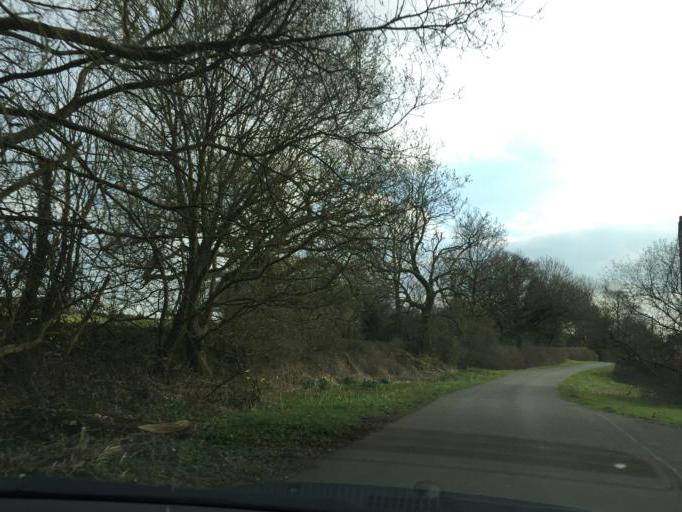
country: GB
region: England
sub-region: Solihull
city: Meriden
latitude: 52.4346
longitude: -1.5878
